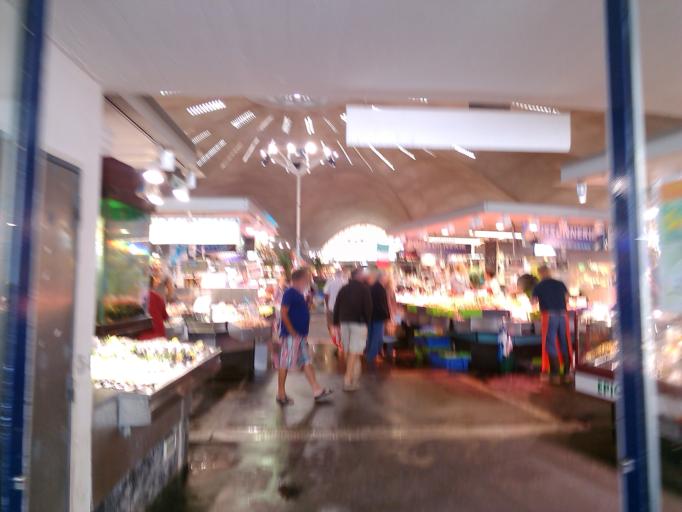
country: FR
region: Poitou-Charentes
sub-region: Departement de la Charente-Maritime
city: Royan
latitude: 45.6277
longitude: -1.0318
